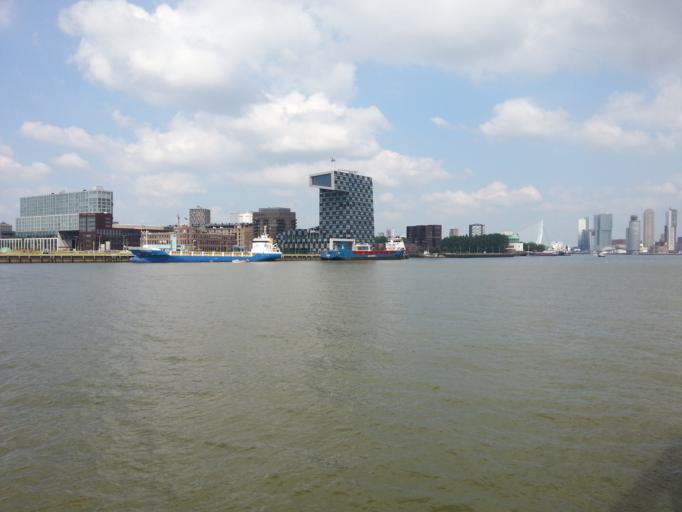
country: NL
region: South Holland
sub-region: Gemeente Rotterdam
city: Delfshaven
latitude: 51.8984
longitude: 4.4567
